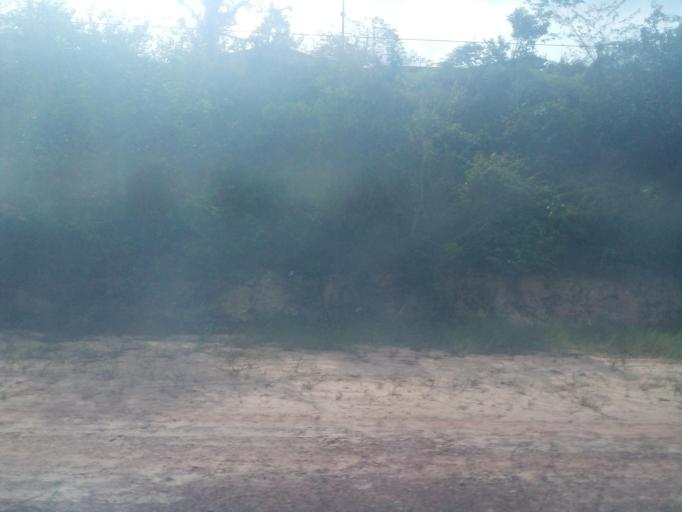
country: BR
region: Maranhao
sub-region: Sao Luis
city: Sao Luis
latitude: -2.7083
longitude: -44.3165
